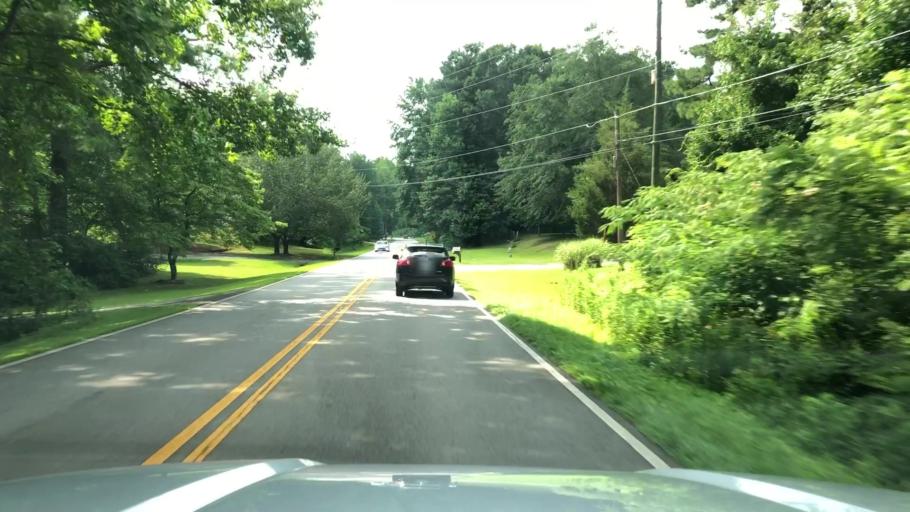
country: US
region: Georgia
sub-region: Paulding County
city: Dallas
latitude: 33.9502
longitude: -84.7742
